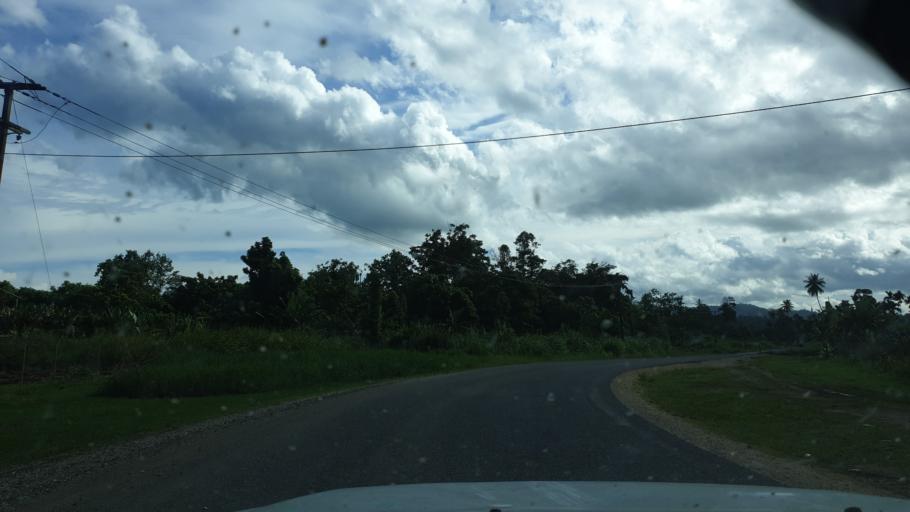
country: PG
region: Madang
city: Madang
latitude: -5.1069
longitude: 145.7928
